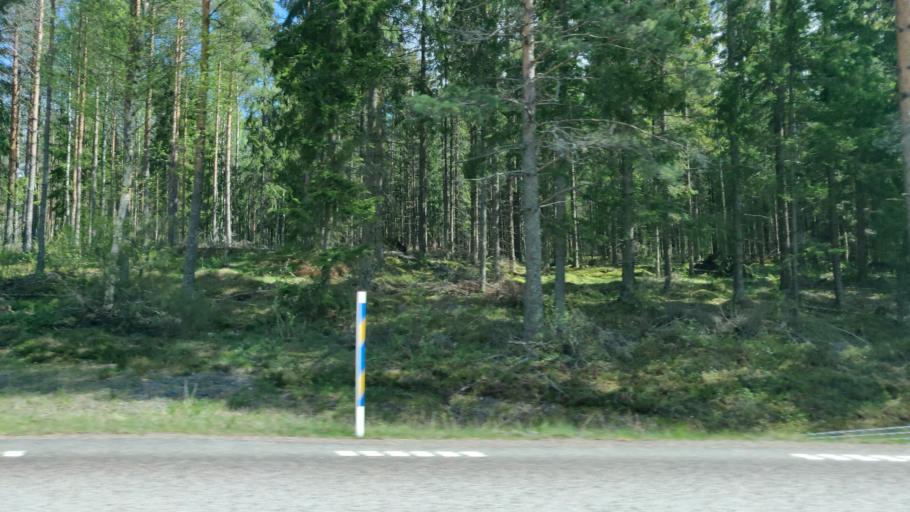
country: SE
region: Vaermland
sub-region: Karlstads Kommun
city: Molkom
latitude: 59.5750
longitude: 13.6678
